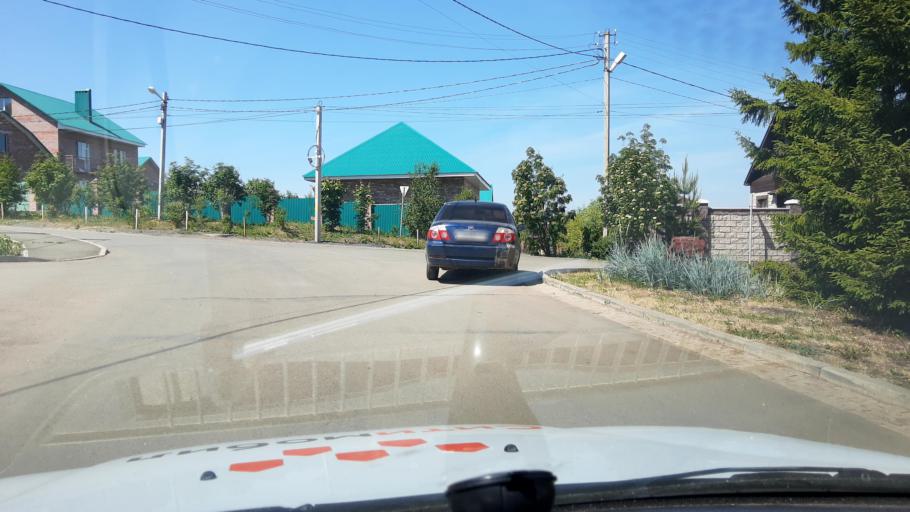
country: RU
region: Bashkortostan
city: Ufa
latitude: 54.6050
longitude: 55.9644
